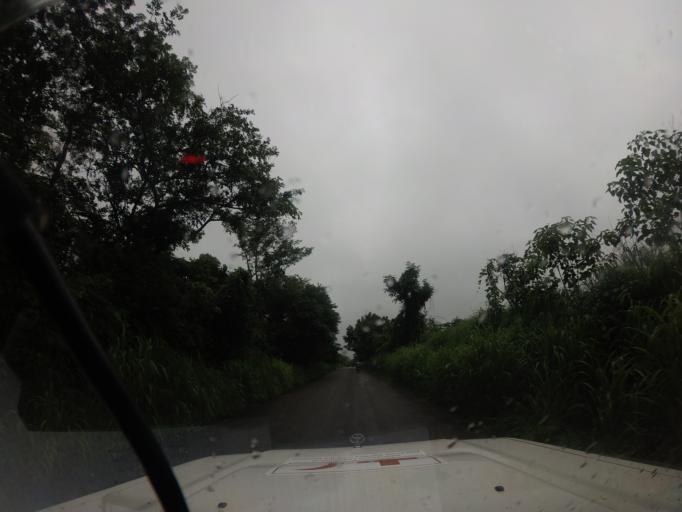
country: SL
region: Northern Province
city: Kabala
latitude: 9.4906
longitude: -11.6089
